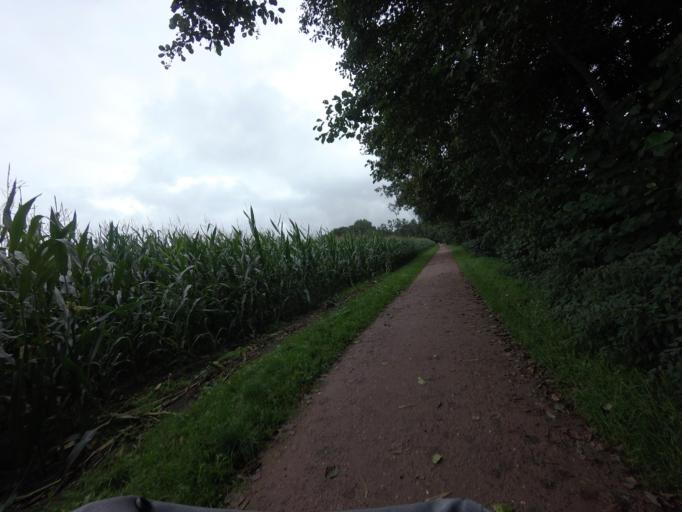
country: DE
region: North Rhine-Westphalia
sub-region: Regierungsbezirk Munster
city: Gronau
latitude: 52.2227
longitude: 7.0244
